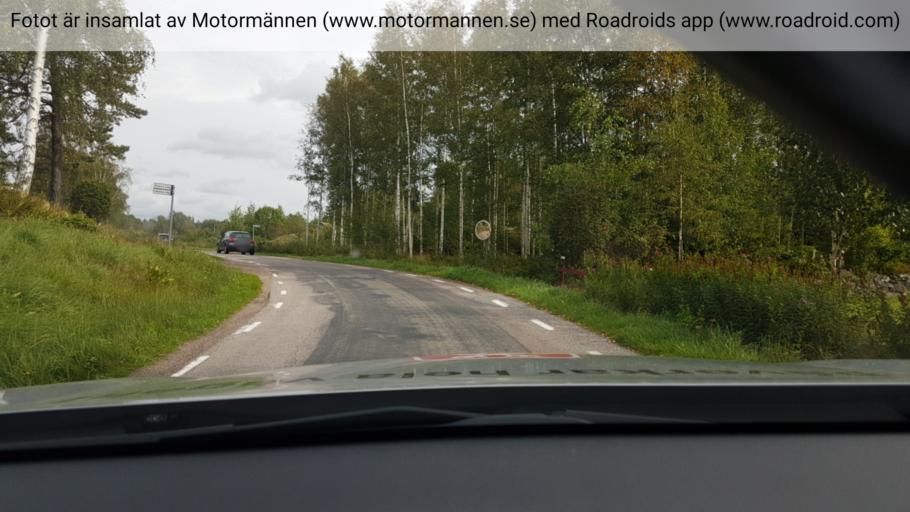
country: SE
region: Vaestra Goetaland
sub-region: Lysekils Kommun
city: Lysekil
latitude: 58.2401
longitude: 11.5520
